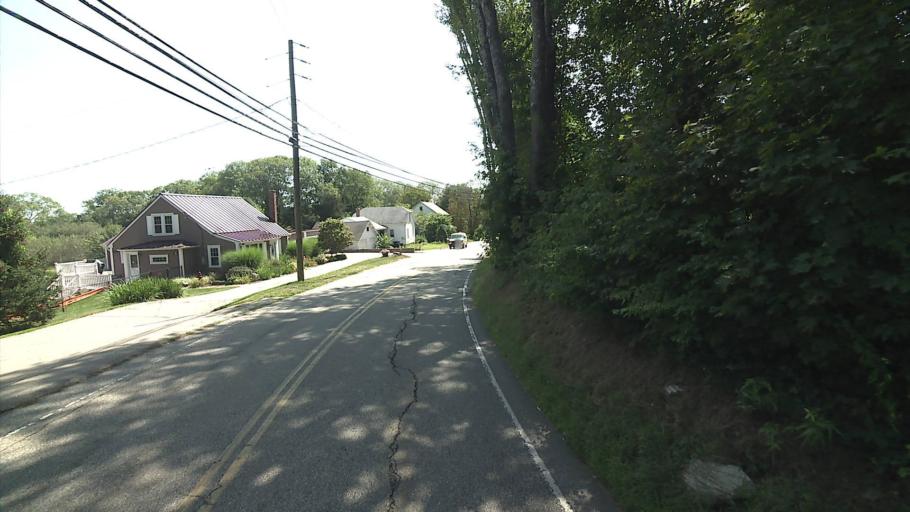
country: US
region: Connecticut
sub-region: New London County
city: Jewett City
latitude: 41.6043
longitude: -71.9960
